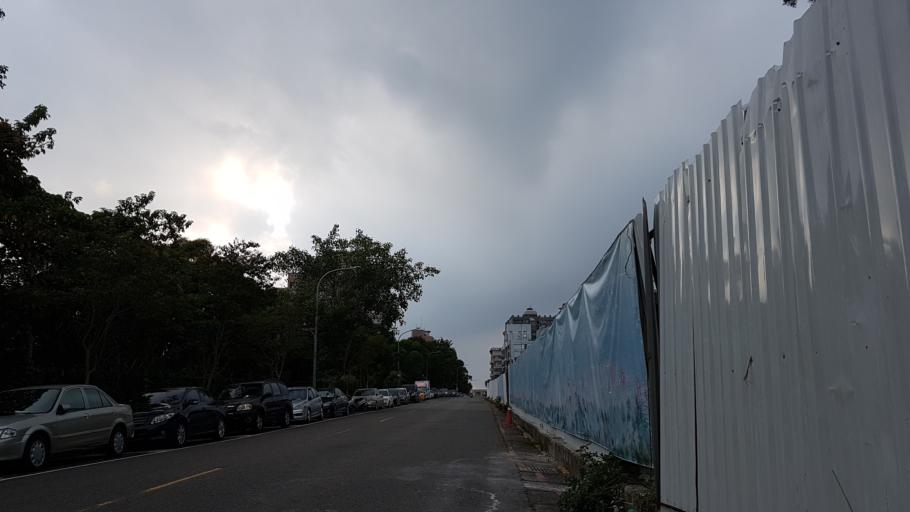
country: TW
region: Taipei
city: Taipei
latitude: 25.0035
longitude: 121.5677
